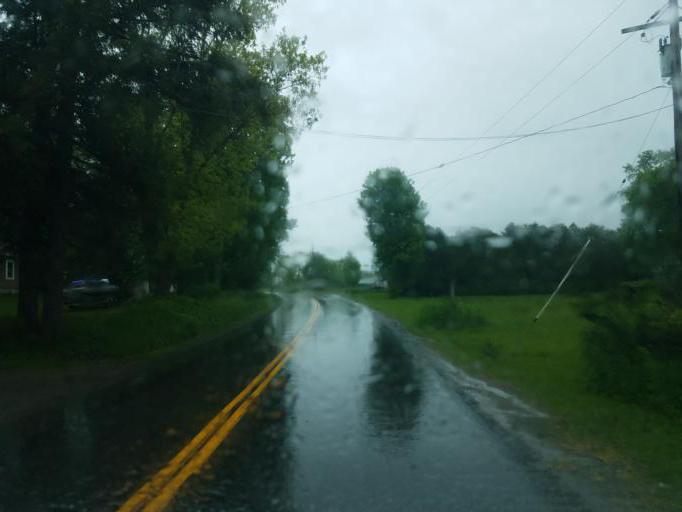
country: US
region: New York
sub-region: Herkimer County
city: Frankfort
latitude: 42.9118
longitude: -75.1478
